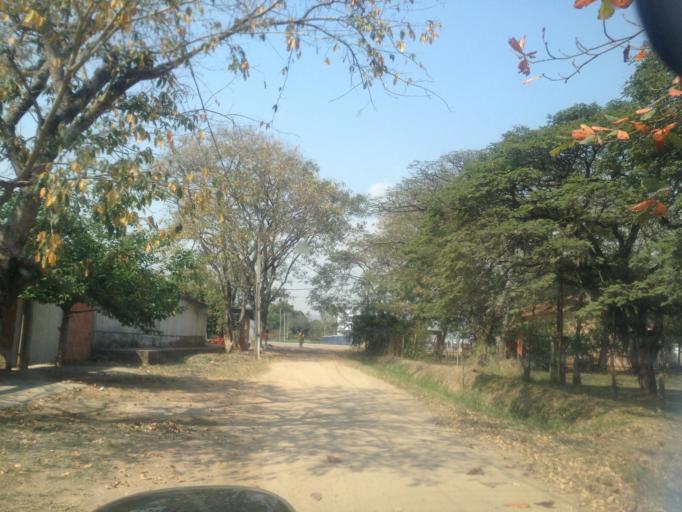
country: BR
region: Rio de Janeiro
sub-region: Porto Real
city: Porto Real
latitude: -22.4327
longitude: -44.3400
